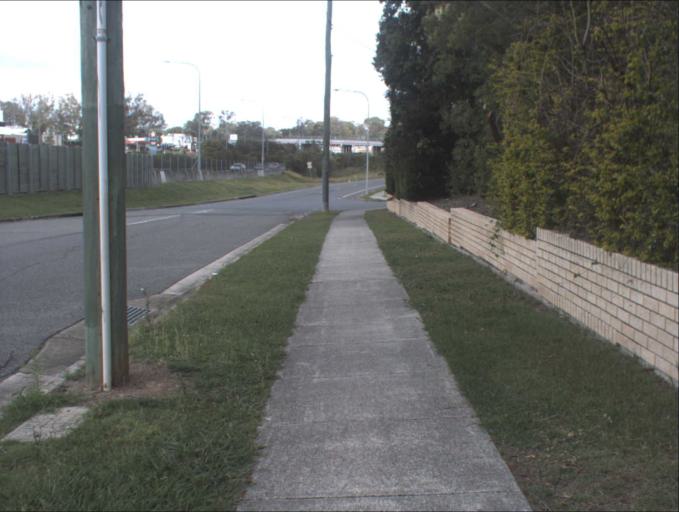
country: AU
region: Queensland
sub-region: Logan
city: Park Ridge South
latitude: -27.6947
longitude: 153.0358
